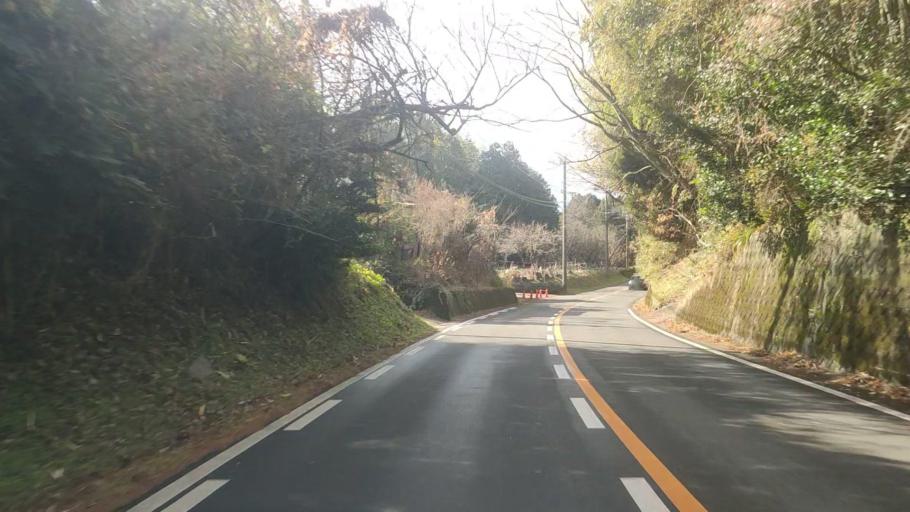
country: JP
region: Kumamoto
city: Hitoyoshi
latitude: 32.2266
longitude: 130.7815
